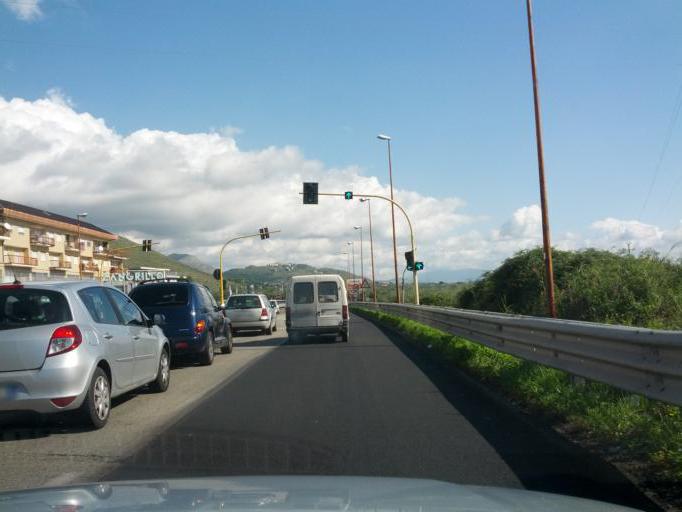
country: IT
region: Latium
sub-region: Provincia di Latina
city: Formia
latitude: 41.2657
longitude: 13.6297
